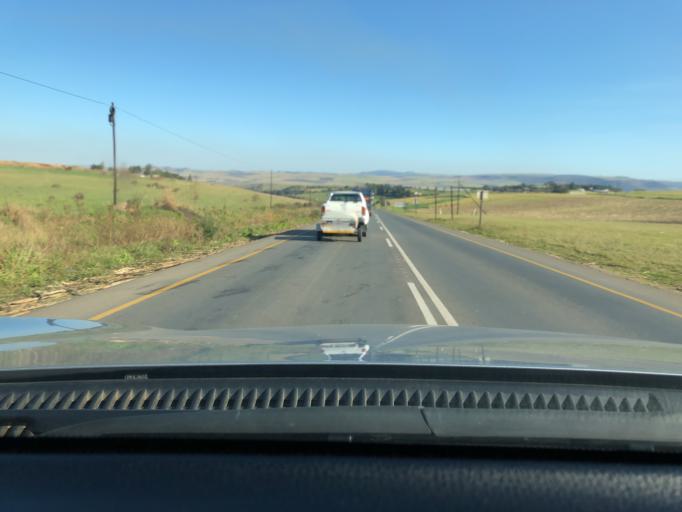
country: ZA
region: KwaZulu-Natal
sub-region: uMgungundlovu District Municipality
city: Camperdown
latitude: -29.7689
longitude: 30.5079
